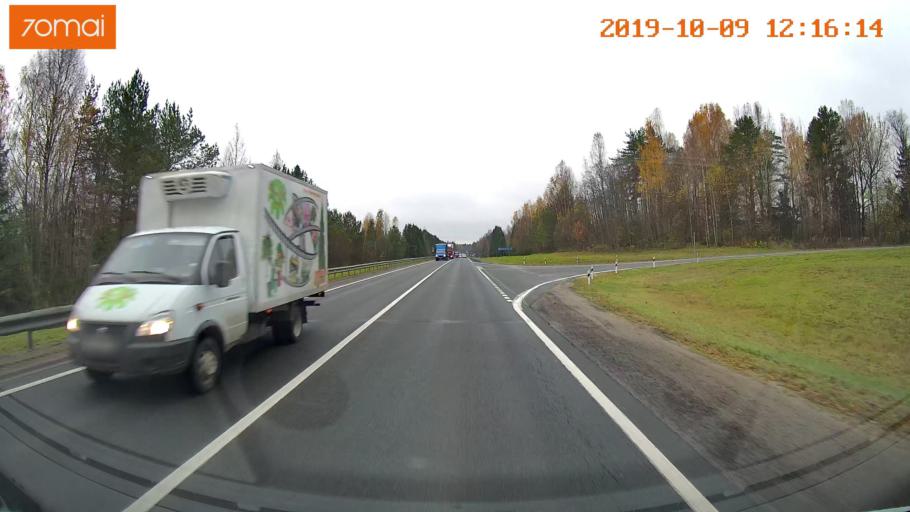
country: RU
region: Jaroslavl
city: Prechistoye
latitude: 58.4716
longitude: 40.3215
